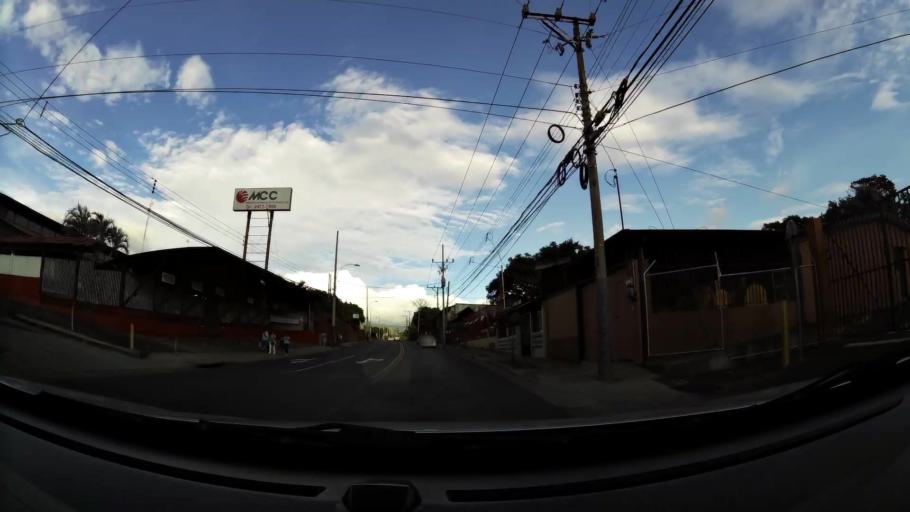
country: CR
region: Heredia
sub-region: Canton de Belen
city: San Antonio
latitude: 10.0044
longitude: -84.1828
